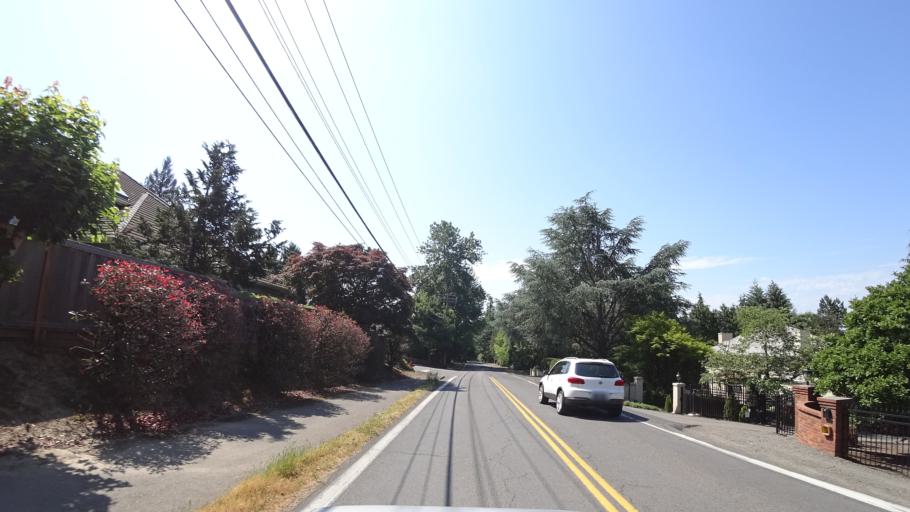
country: US
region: Oregon
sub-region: Washington County
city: Durham
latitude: 45.4231
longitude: -122.7220
